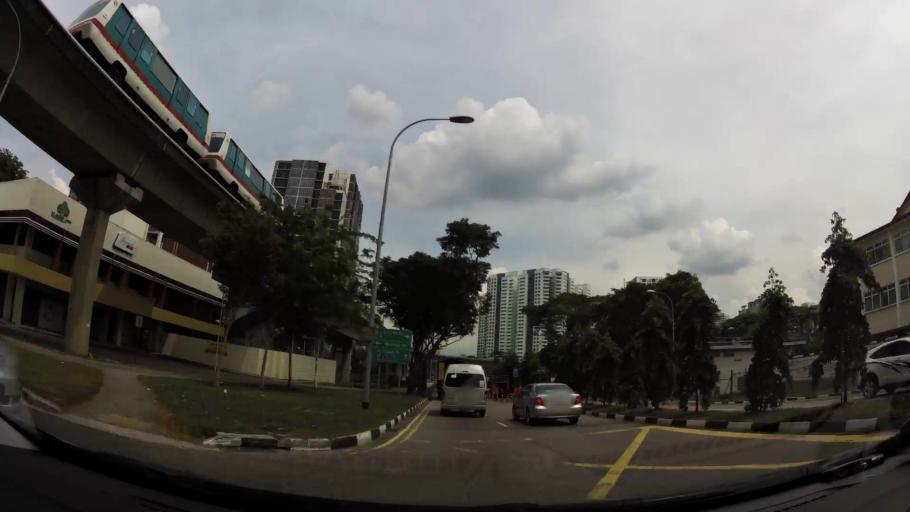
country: MY
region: Johor
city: Johor Bahru
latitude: 1.3789
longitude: 103.7591
